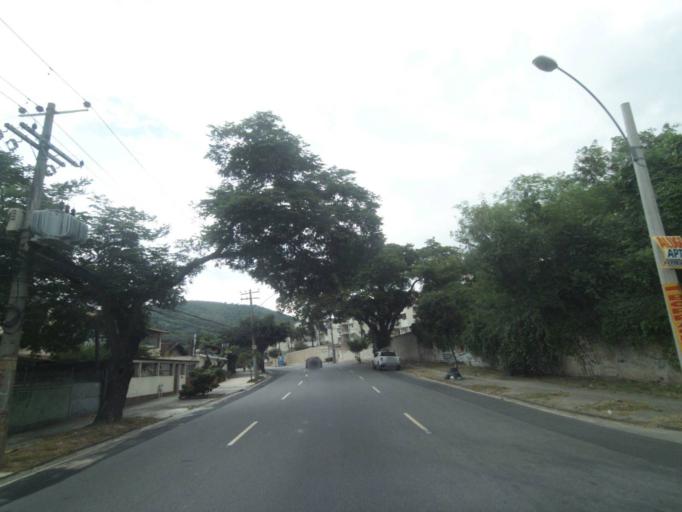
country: BR
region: Rio de Janeiro
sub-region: Nilopolis
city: Nilopolis
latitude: -22.8884
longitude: -43.3944
